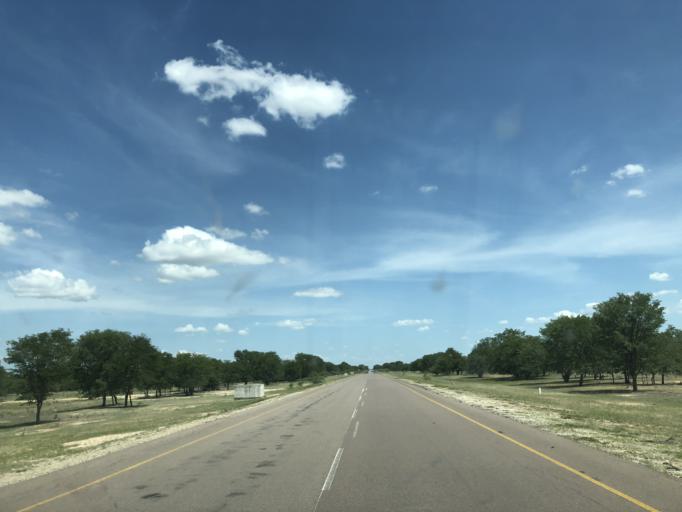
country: AO
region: Cunene
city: Ondjiva
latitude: -16.8386
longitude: 15.4583
